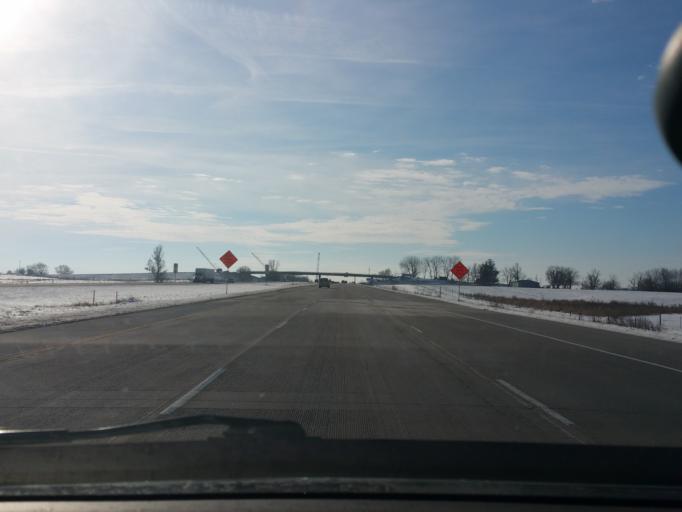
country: US
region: Iowa
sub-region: Polk County
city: West Des Moines
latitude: 41.5102
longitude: -93.7807
